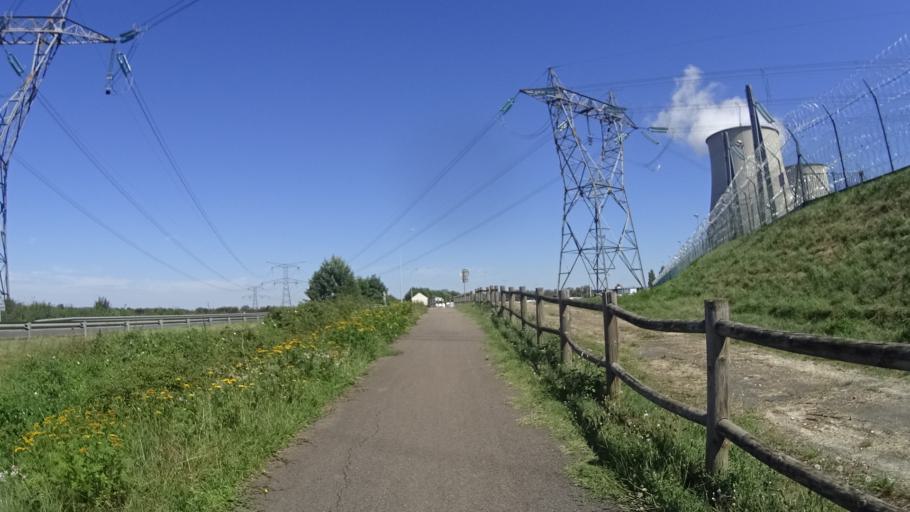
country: FR
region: Centre
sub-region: Departement du Cher
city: Belleville-sur-Loire
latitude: 47.5071
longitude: 2.8679
